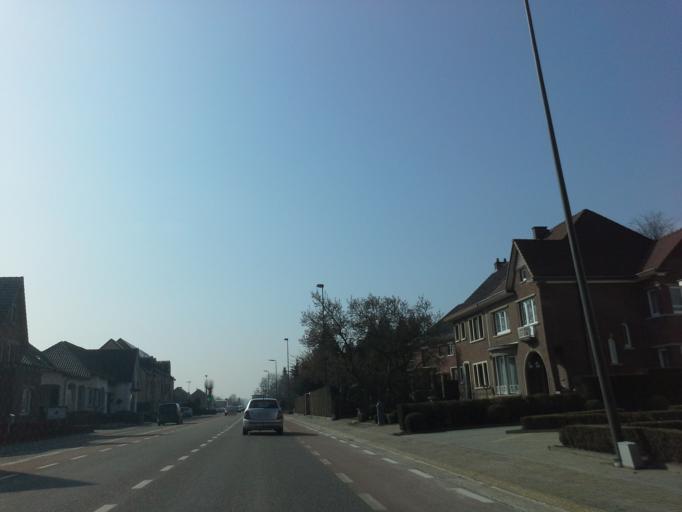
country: BE
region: Flanders
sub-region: Provincie Limburg
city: Hoeselt
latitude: 50.8482
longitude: 5.4894
